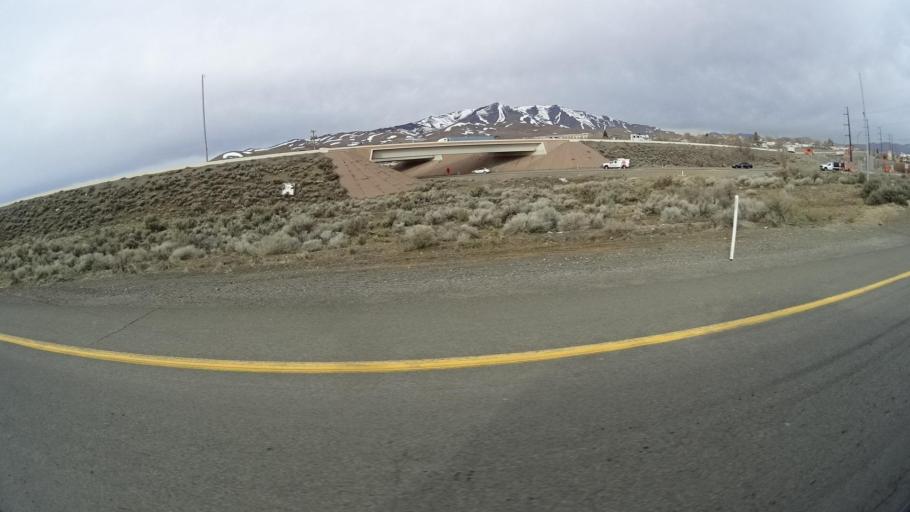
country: US
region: Nevada
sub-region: Washoe County
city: Golden Valley
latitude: 39.6007
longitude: -119.8360
